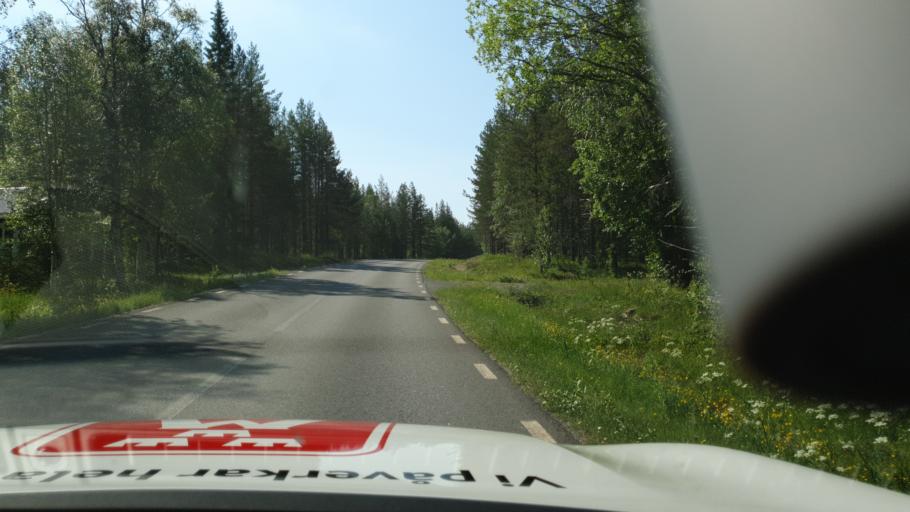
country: SE
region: Vaesterbotten
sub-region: Skelleftea Kommun
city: Langsele
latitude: 64.9933
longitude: 20.0896
